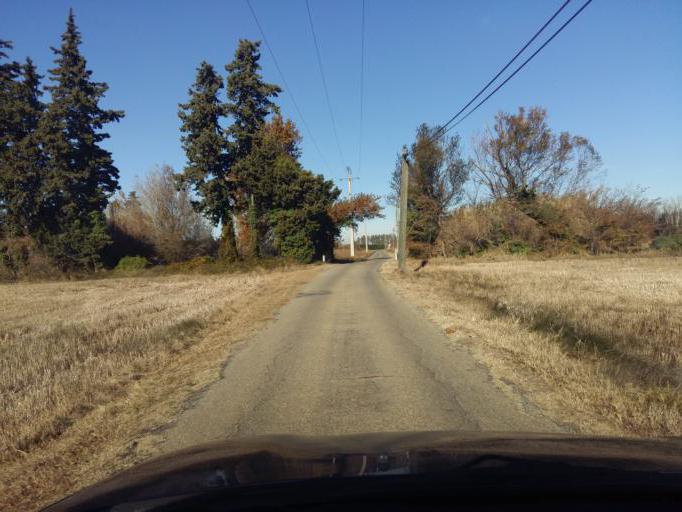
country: FR
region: Provence-Alpes-Cote d'Azur
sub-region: Departement du Vaucluse
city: Althen-des-Paluds
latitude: 44.0297
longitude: 4.9539
